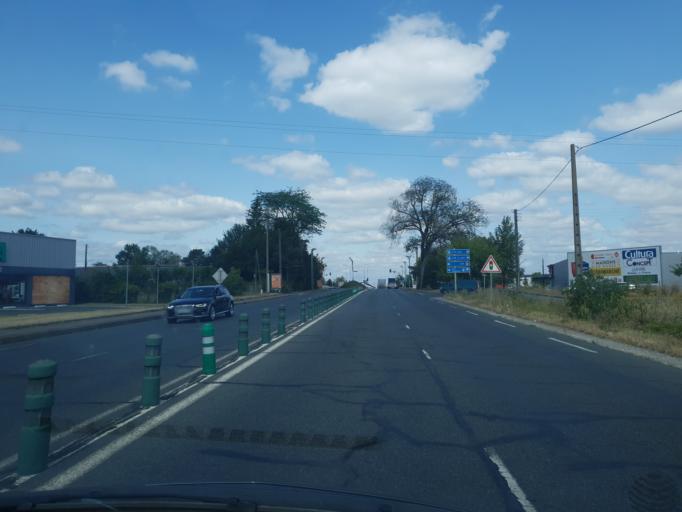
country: FR
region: Centre
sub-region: Departement d'Indre-et-Loire
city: Chambray-les-Tours
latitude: 47.3423
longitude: 0.7030
